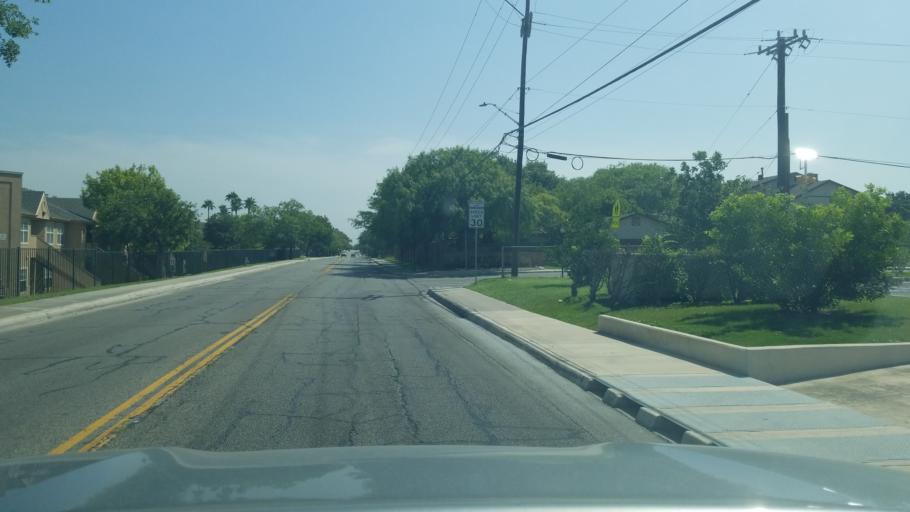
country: US
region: Texas
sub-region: Bexar County
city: Hollywood Park
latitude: 29.5671
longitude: -98.4764
